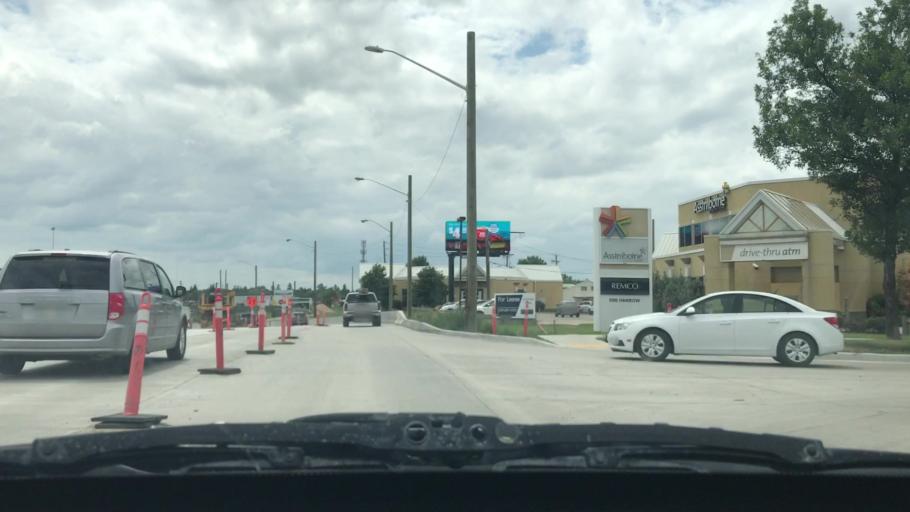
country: CA
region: Manitoba
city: Winnipeg
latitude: 49.8563
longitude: -97.1527
